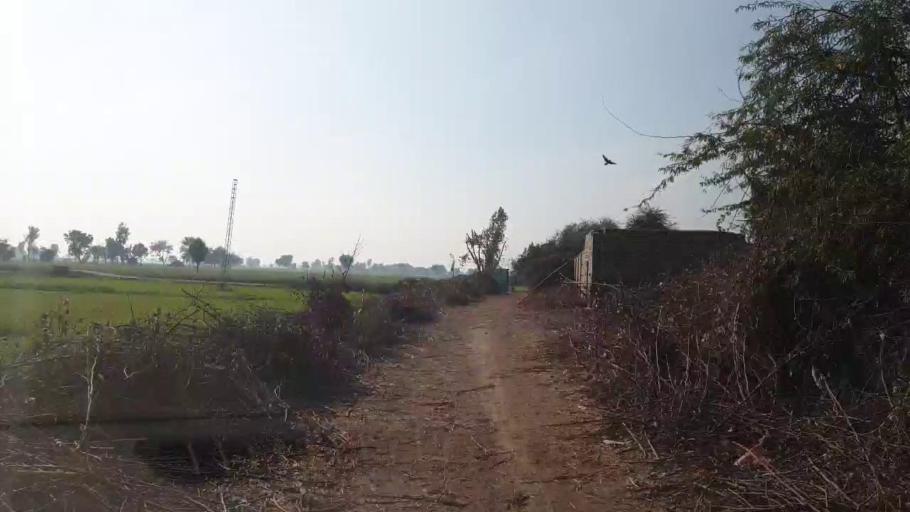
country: PK
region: Sindh
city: Shahdadpur
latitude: 25.9898
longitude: 68.6249
